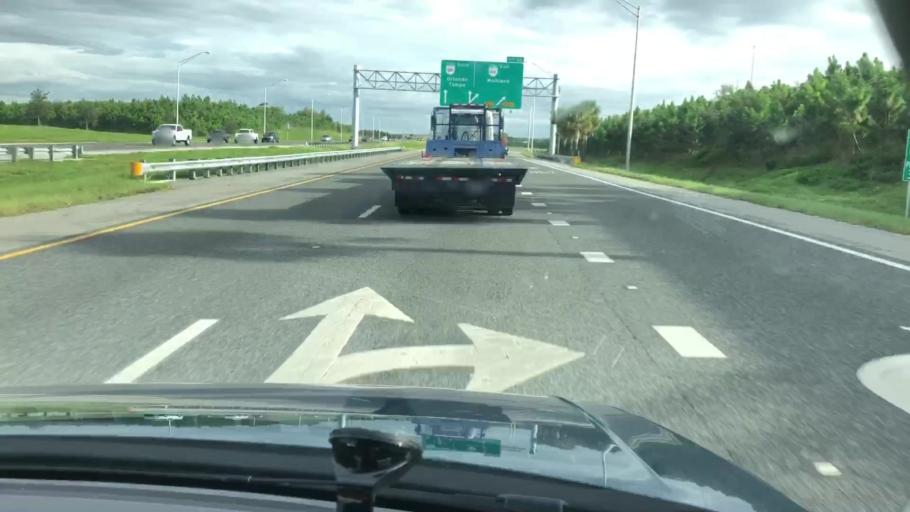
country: US
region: Florida
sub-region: Orange County
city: Paradise Heights
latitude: 28.6582
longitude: -81.5503
